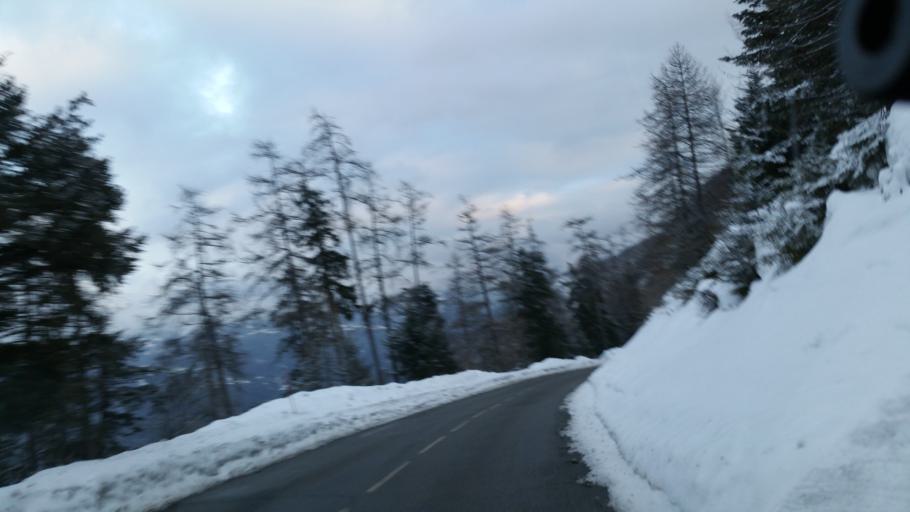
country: FR
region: Rhone-Alpes
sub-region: Departement de la Savoie
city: Villargondran
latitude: 45.2368
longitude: 6.3992
